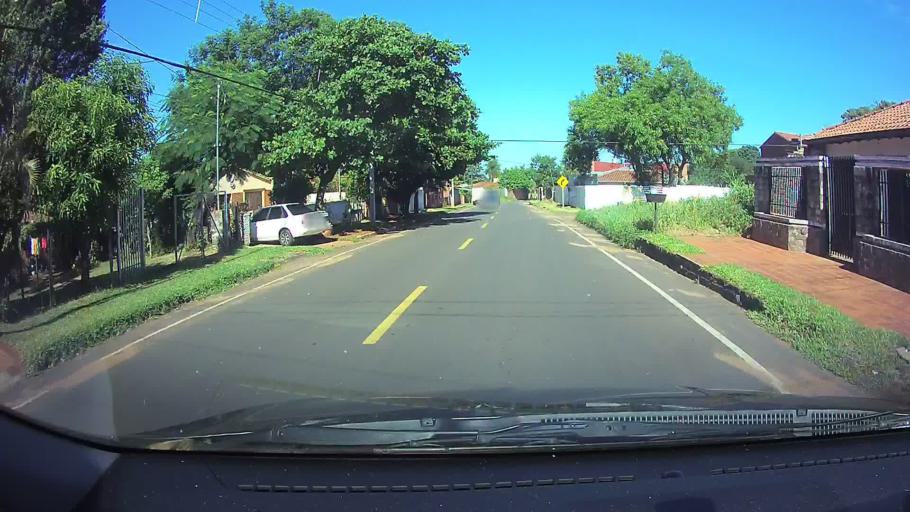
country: PY
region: Central
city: San Lorenzo
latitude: -25.2785
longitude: -57.5079
